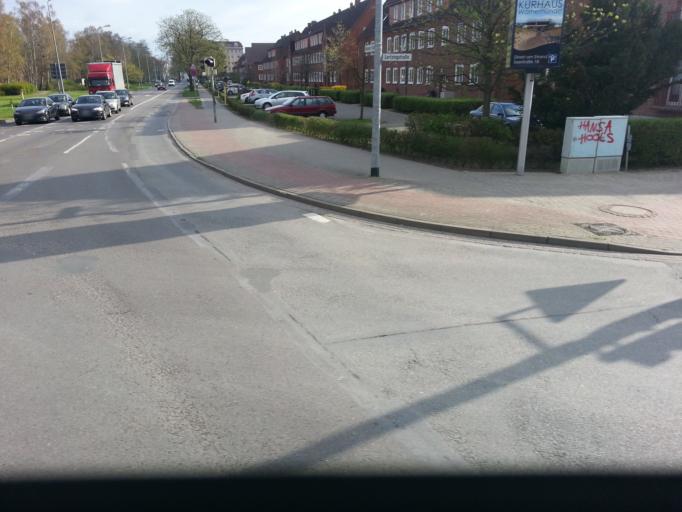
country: DE
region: Mecklenburg-Vorpommern
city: Warnemuende
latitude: 54.1706
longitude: 12.0827
